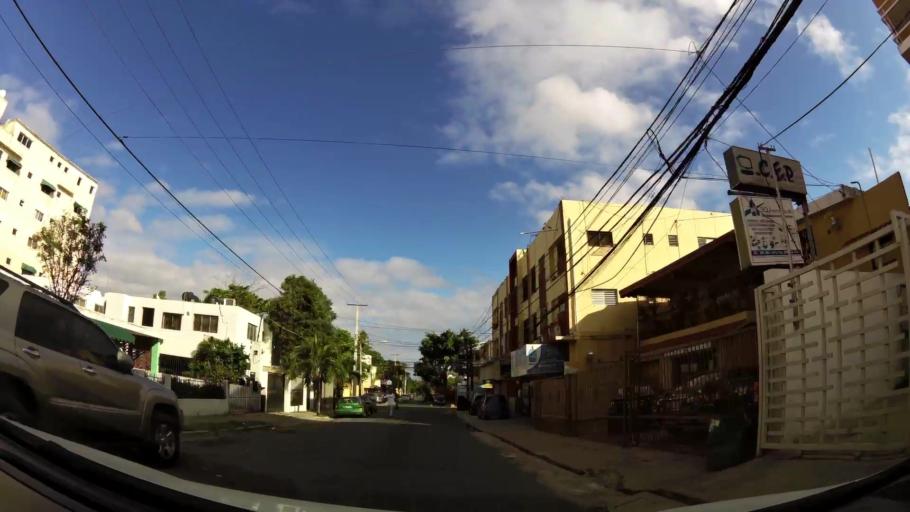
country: DO
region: Nacional
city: Bella Vista
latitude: 18.4613
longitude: -69.9511
